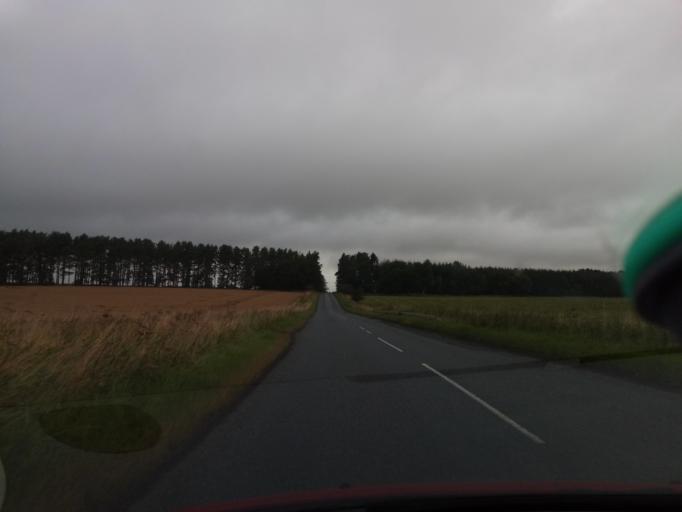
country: GB
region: Scotland
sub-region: The Scottish Borders
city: Earlston
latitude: 55.6616
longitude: -2.5513
